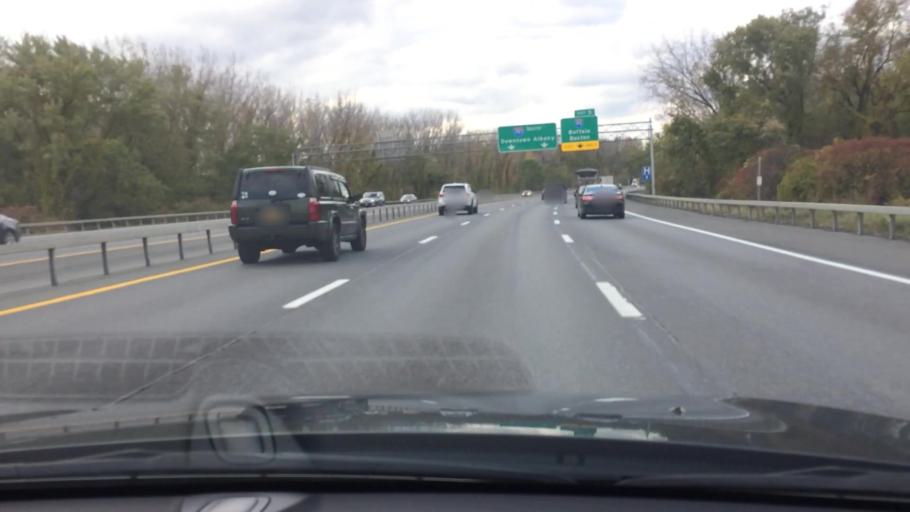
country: US
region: New York
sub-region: Albany County
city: Menands
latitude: 42.6754
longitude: -73.7256
